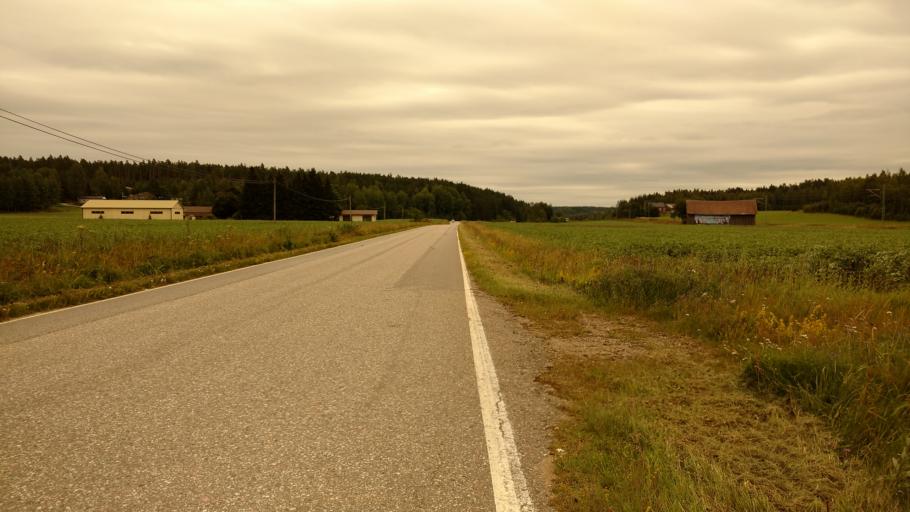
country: FI
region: Varsinais-Suomi
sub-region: Loimaa
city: Marttila
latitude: 60.4165
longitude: 22.8613
